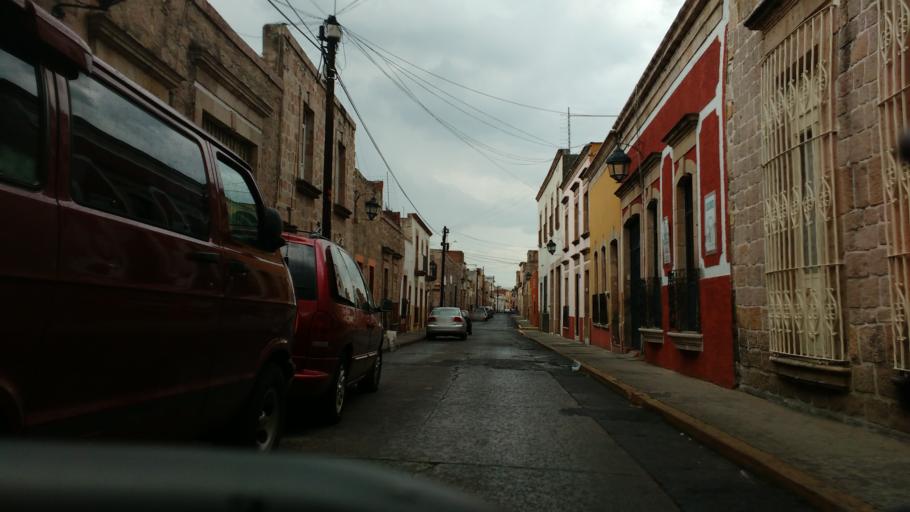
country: MX
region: Michoacan
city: Morelia
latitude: 19.7052
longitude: -101.1854
